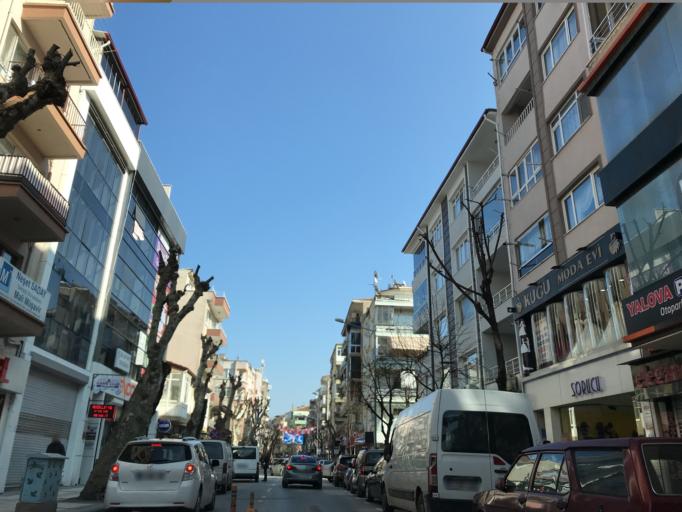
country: TR
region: Yalova
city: Yalova
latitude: 40.6558
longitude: 29.2716
